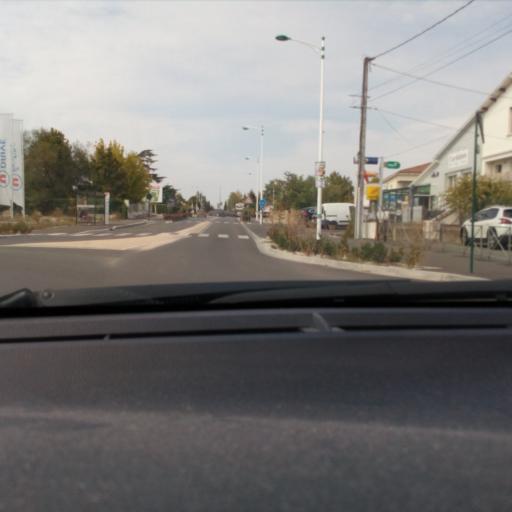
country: FR
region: Poitou-Charentes
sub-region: Departement de la Charente
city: Saint-Yrieix-sur-Charente
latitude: 45.6731
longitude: 0.1259
